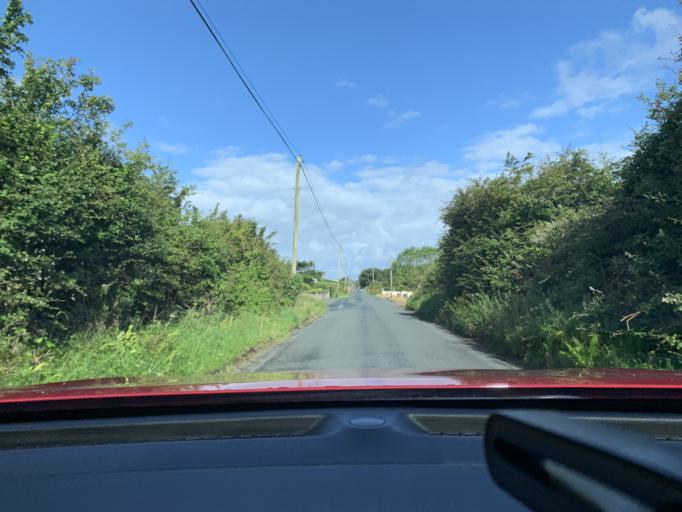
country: IE
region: Connaught
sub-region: Sligo
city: Strandhill
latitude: 54.3930
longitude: -8.5504
